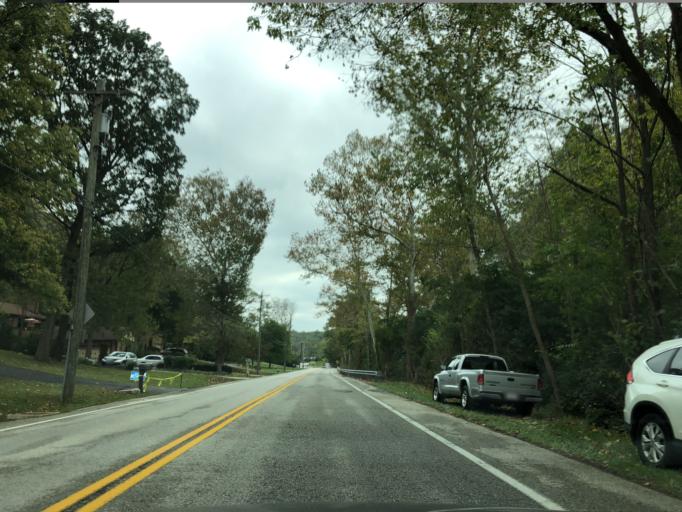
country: US
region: Ohio
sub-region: Hamilton County
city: The Village of Indian Hill
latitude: 39.2520
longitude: -84.3011
